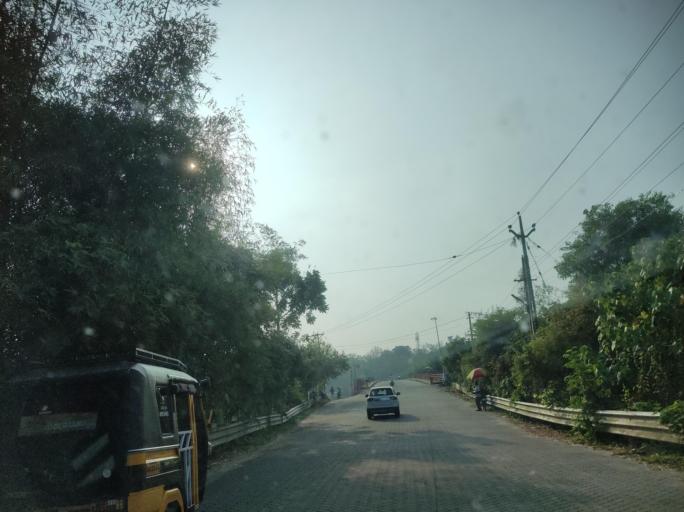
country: IN
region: Kerala
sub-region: Kottayam
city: Kottayam
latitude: 9.5632
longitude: 76.5106
